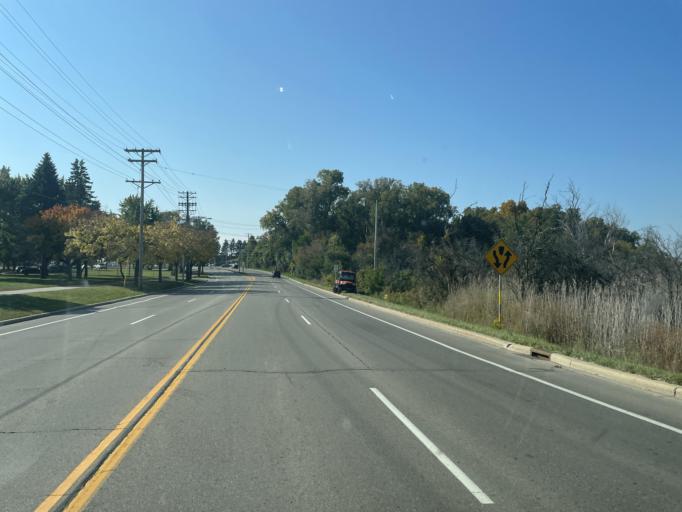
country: US
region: Wisconsin
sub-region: Dane County
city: Madison
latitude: 43.0466
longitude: -89.4028
